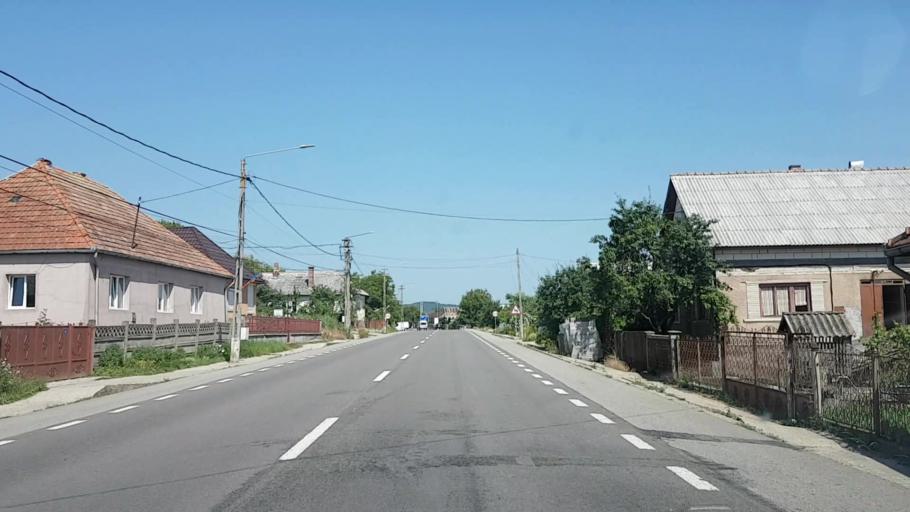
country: RO
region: Bistrita-Nasaud
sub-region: Comuna Uriu
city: Uriu
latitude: 47.2011
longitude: 24.0566
